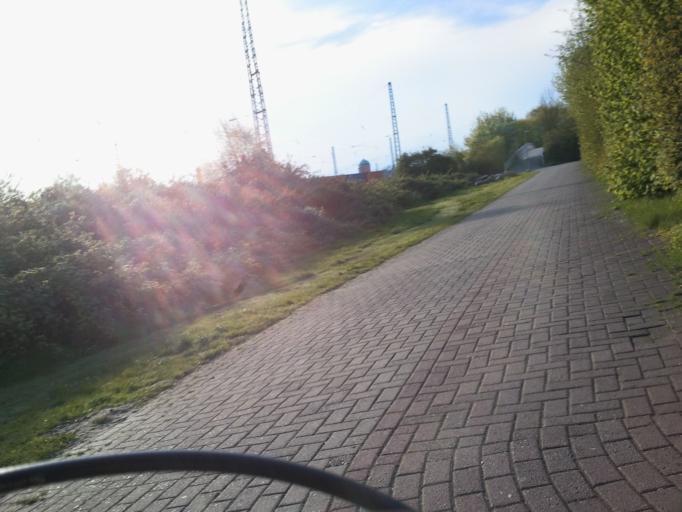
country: DE
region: Lower Saxony
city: Nienburg
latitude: 52.6423
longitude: 9.2228
